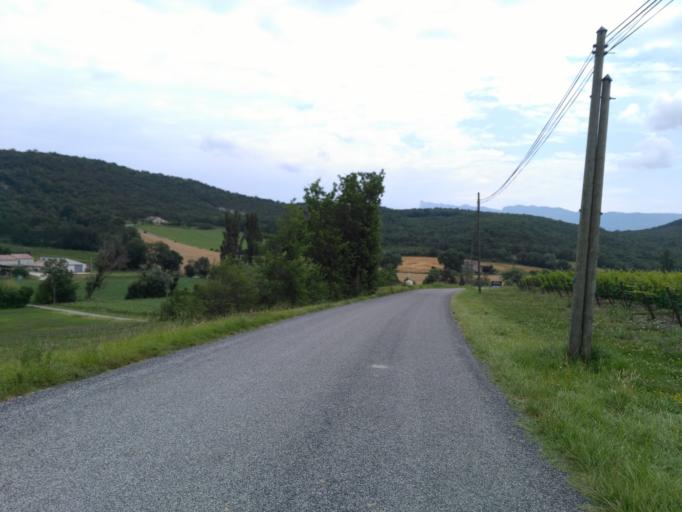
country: FR
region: Rhone-Alpes
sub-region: Departement de la Drome
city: Aouste-sur-Sye
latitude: 44.7567
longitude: 5.1165
